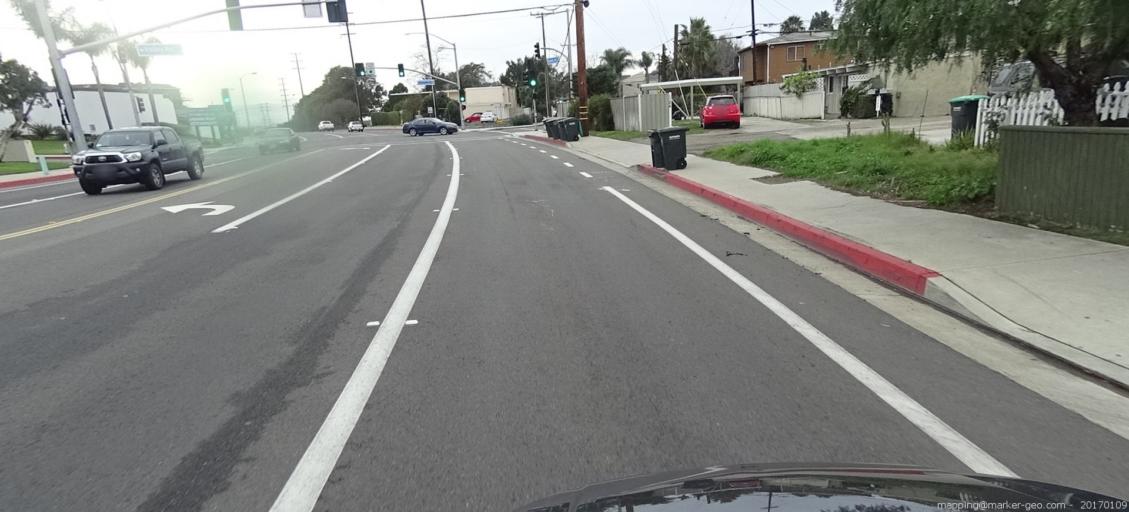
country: US
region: California
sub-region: Orange County
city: Costa Mesa
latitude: 33.6524
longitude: -117.9456
